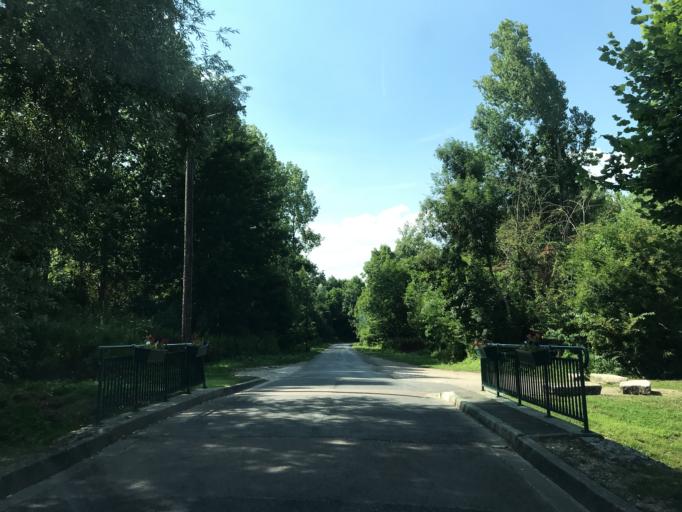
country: FR
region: Haute-Normandie
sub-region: Departement de l'Eure
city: Gasny
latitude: 49.0782
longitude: 1.5899
